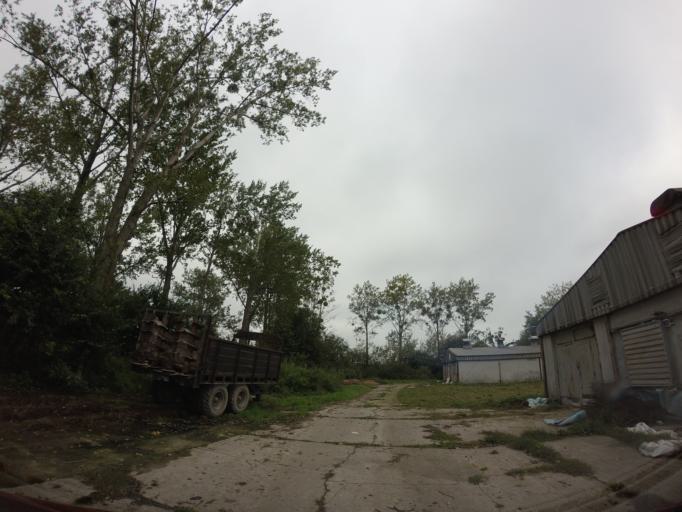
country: PL
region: West Pomeranian Voivodeship
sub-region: Powiat choszczenski
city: Krzecin
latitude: 53.0287
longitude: 15.4565
